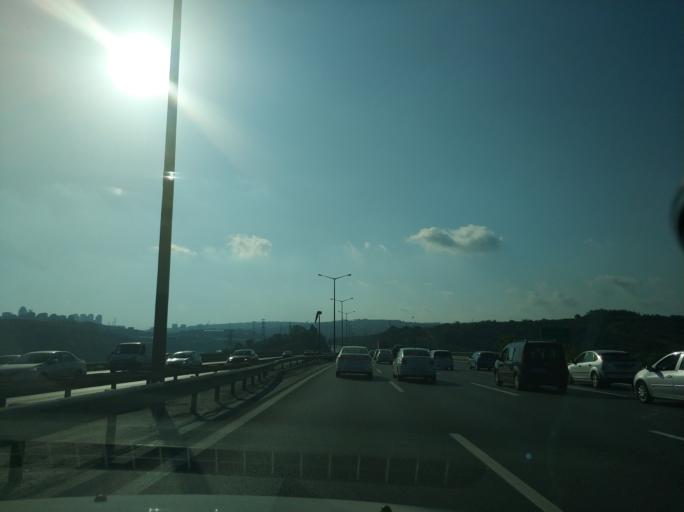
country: TR
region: Istanbul
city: Sisli
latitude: 41.0924
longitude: 28.9367
